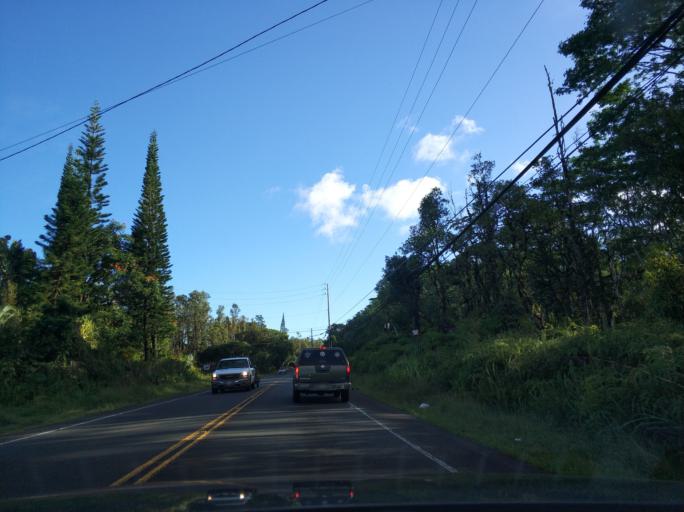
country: US
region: Hawaii
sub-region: Hawaii County
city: Leilani Estates
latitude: 19.4624
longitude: -154.9410
